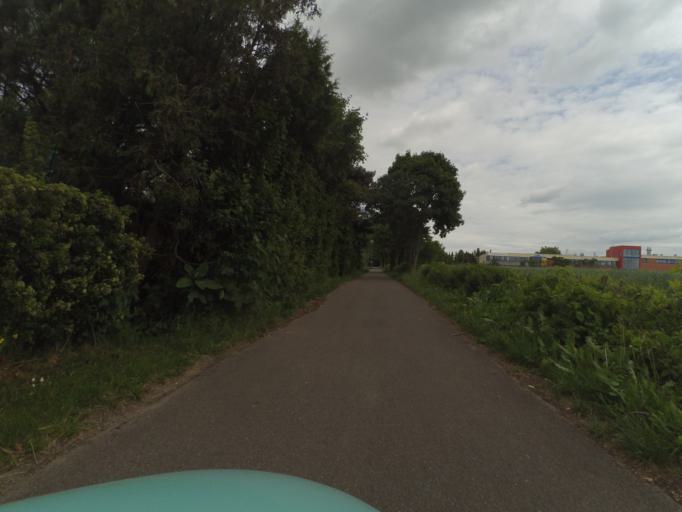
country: DE
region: Lower Saxony
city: Hagenburg
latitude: 52.4553
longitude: 9.3798
